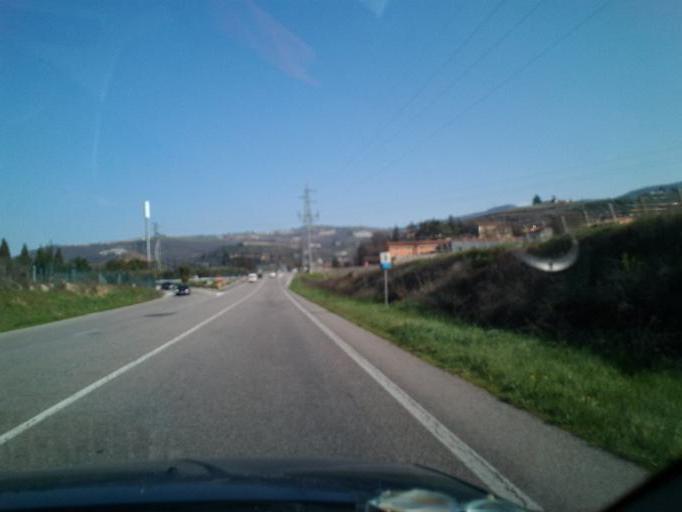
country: IT
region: Veneto
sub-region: Provincia di Verona
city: Grezzana
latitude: 45.5141
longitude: 11.0217
